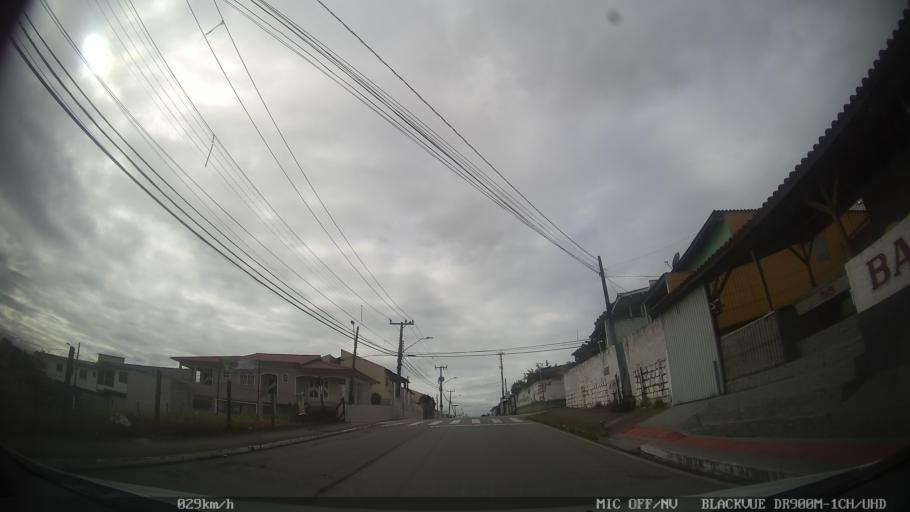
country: BR
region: Santa Catarina
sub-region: Sao Jose
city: Campinas
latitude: -27.5667
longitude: -48.6281
